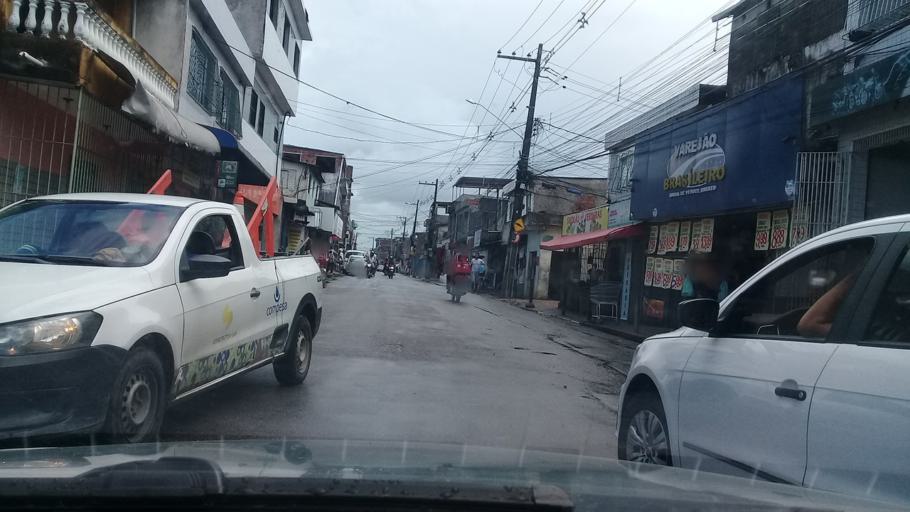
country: BR
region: Pernambuco
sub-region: Jaboatao Dos Guararapes
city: Jaboatao dos Guararapes
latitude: -8.1115
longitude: -34.9575
